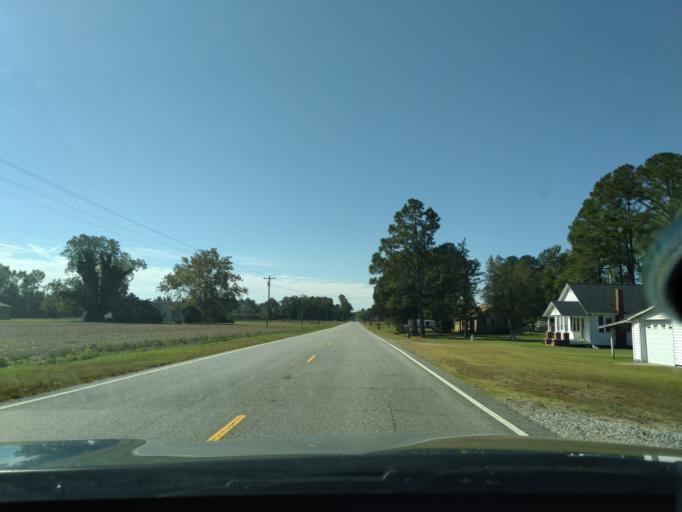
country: US
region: North Carolina
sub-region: Washington County
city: Plymouth
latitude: 35.6894
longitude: -76.7737
